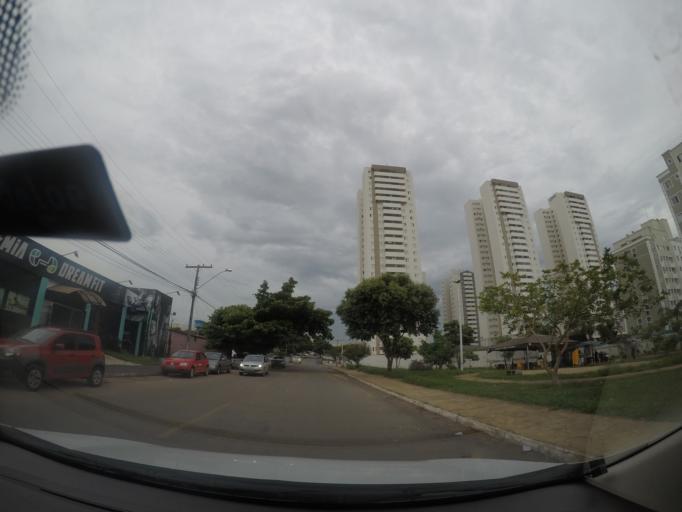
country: BR
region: Goias
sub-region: Goiania
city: Goiania
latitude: -16.6540
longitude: -49.2406
